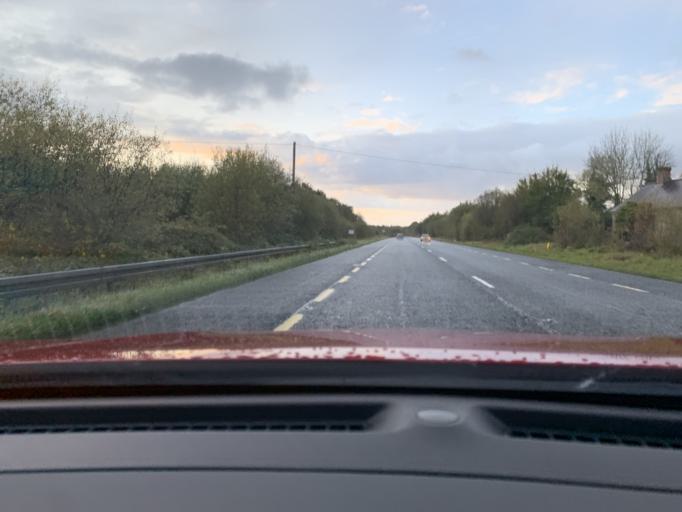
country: IE
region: Connaught
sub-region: County Leitrim
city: Carrick-on-Shannon
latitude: 53.9545
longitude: -8.1570
